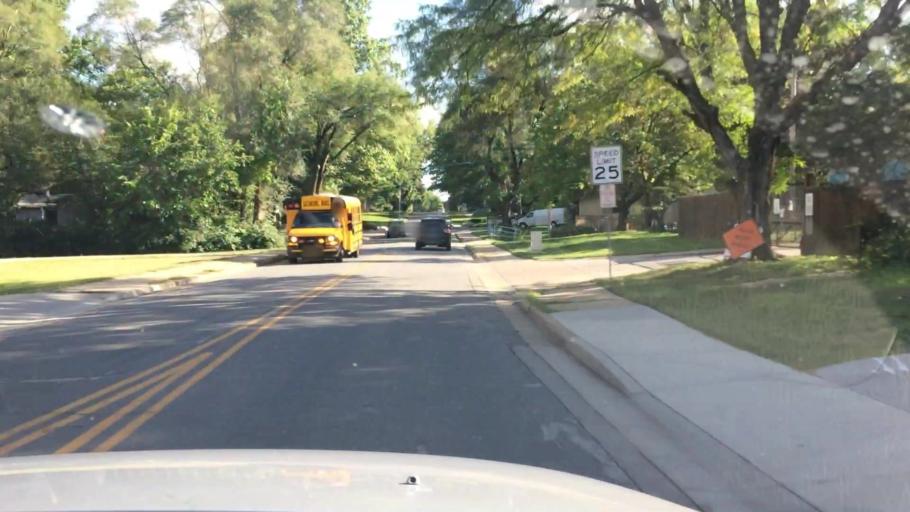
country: US
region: Kansas
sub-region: Johnson County
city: Overland Park
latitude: 38.9925
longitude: -94.6584
